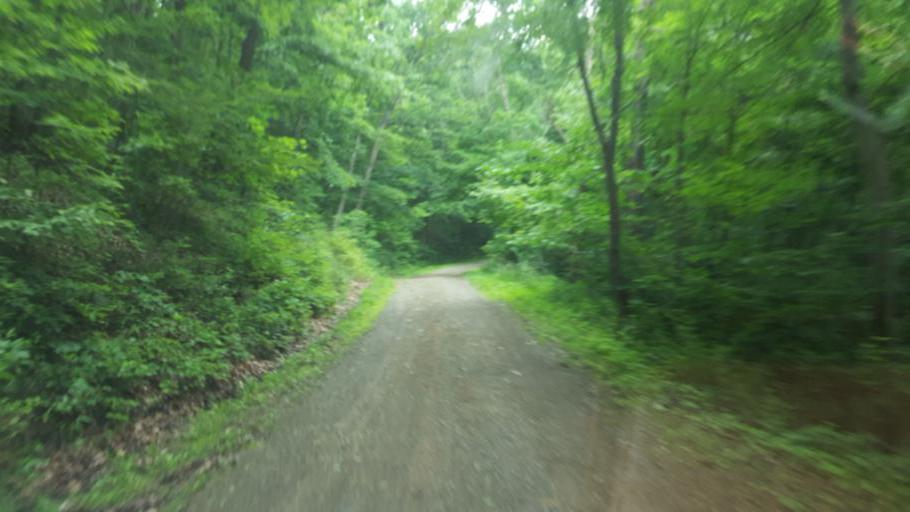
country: US
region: Ohio
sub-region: Columbiana County
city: Salineville
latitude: 40.5541
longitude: -80.8038
